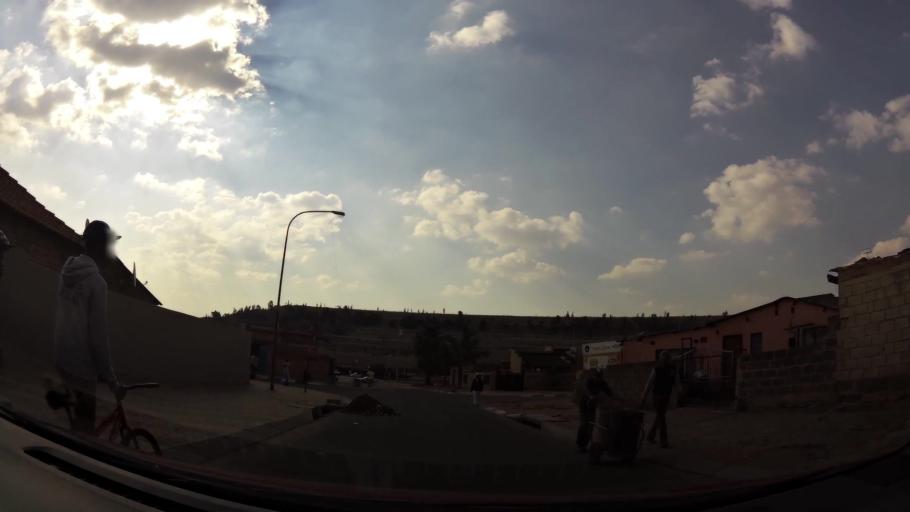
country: ZA
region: Gauteng
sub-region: City of Johannesburg Metropolitan Municipality
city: Soweto
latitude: -26.2343
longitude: 27.9494
